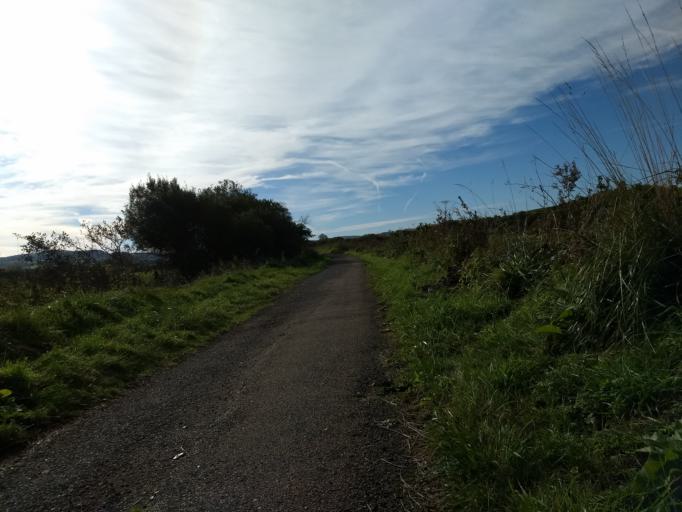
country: GB
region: England
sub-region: Isle of Wight
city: Newchurch
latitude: 50.6598
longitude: -1.2403
